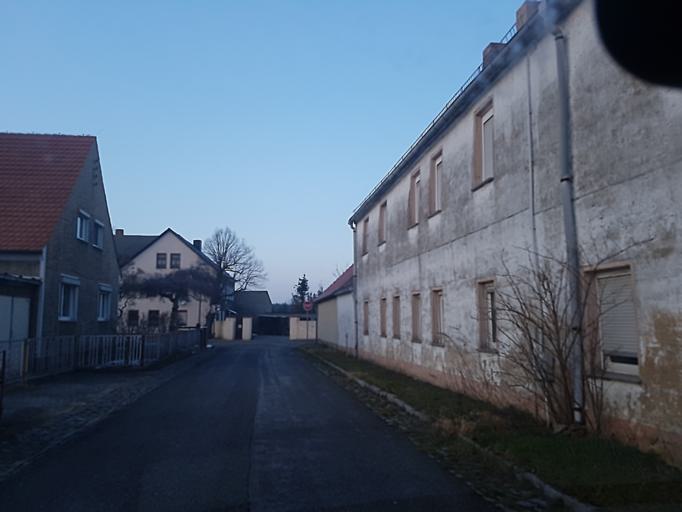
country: DE
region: Brandenburg
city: Muhlberg
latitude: 51.4691
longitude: 13.2947
